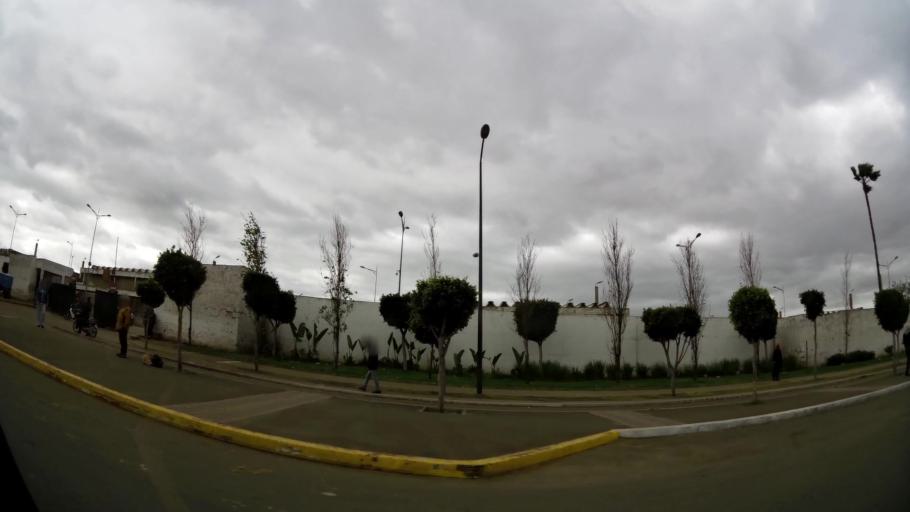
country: MA
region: Grand Casablanca
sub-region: Casablanca
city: Casablanca
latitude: 33.5552
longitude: -7.5568
